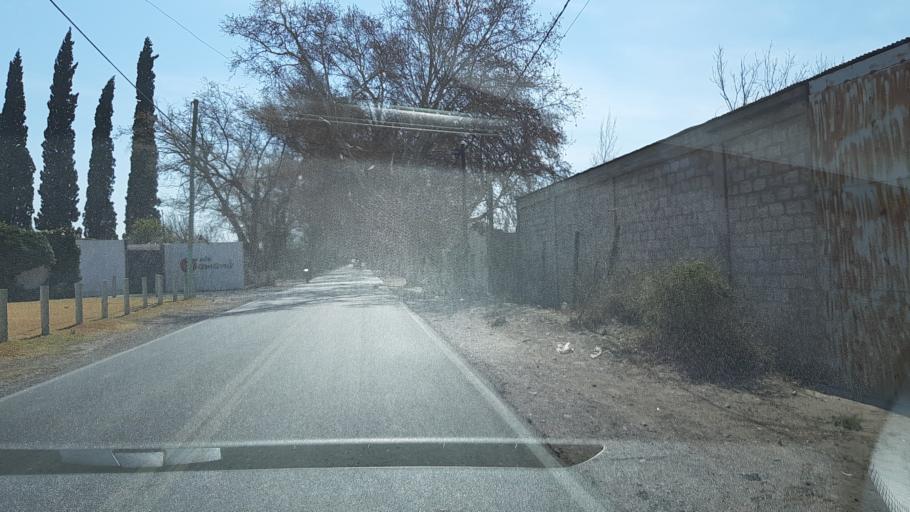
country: AR
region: San Juan
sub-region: Departamento de Rivadavia
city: Rivadavia
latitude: -31.5311
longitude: -68.6186
